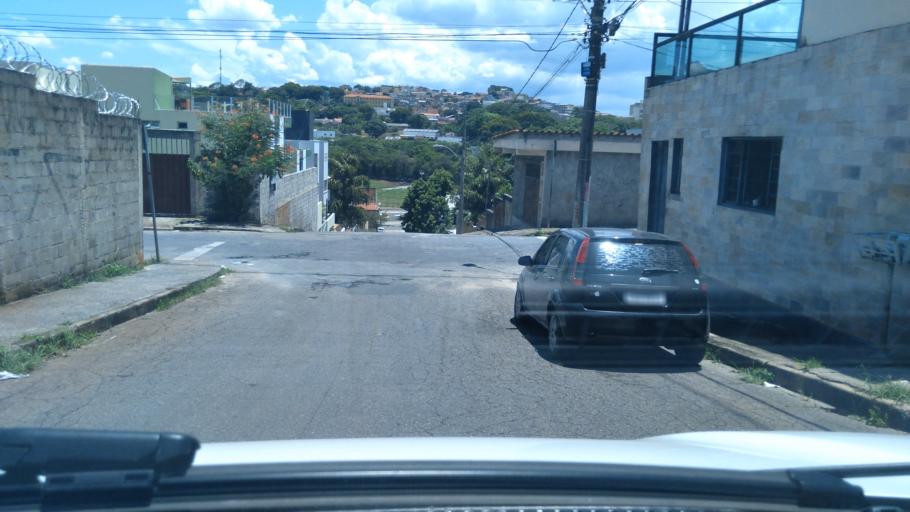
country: BR
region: Minas Gerais
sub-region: Contagem
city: Contagem
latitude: -19.9342
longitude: -43.9989
